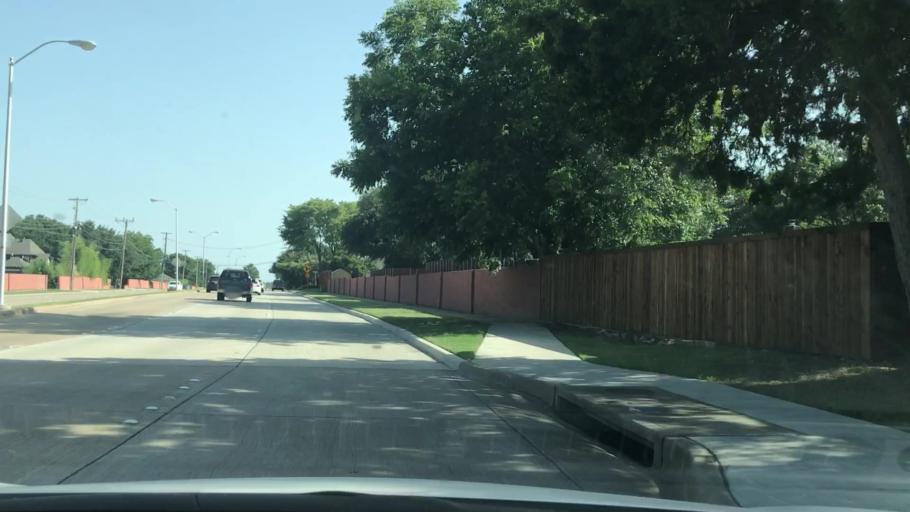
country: US
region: Texas
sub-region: Collin County
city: Plano
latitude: 33.0473
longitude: -96.7533
